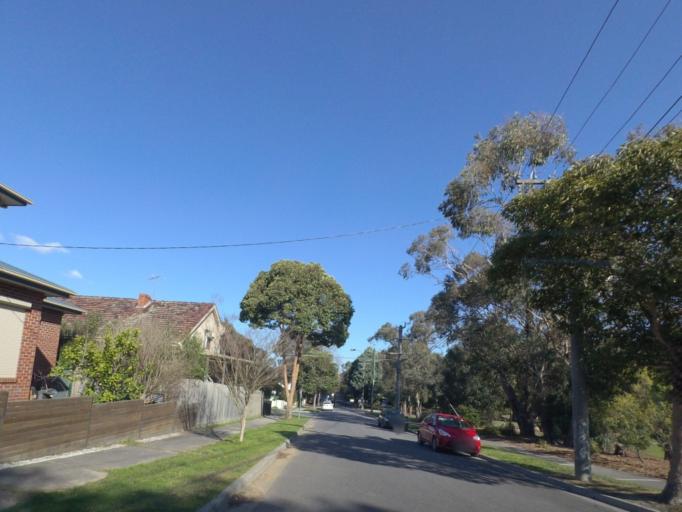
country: AU
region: Victoria
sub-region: Maroondah
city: Ringwood East
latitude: -37.8214
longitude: 145.2343
